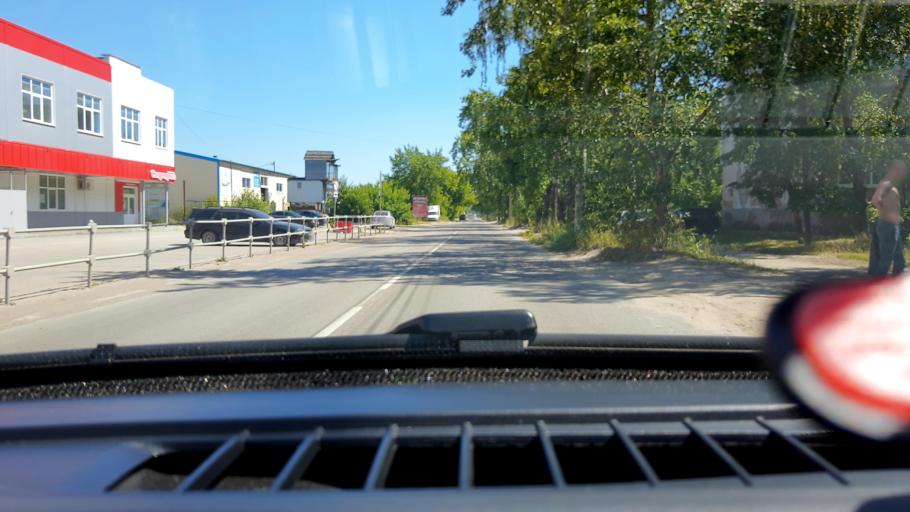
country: RU
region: Nizjnij Novgorod
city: Dzerzhinsk
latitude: 56.2551
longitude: 43.4703
